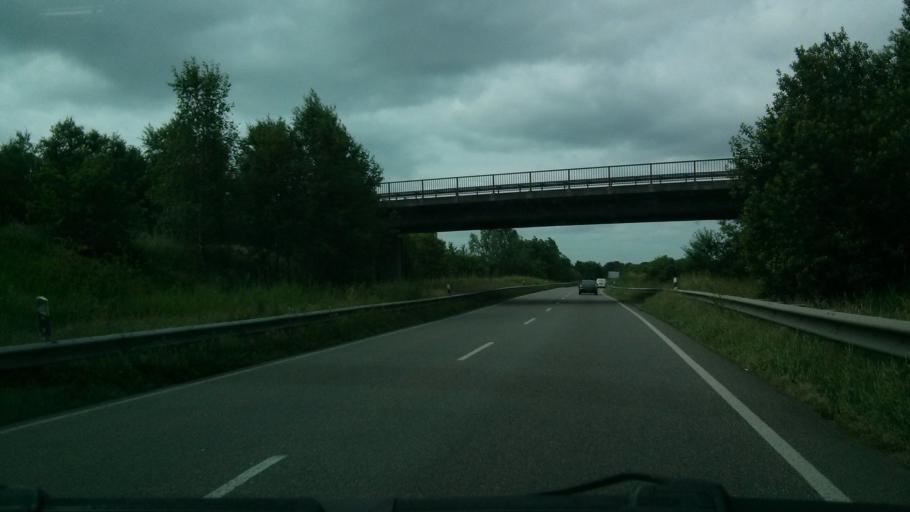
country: DE
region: Lower Saxony
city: Driftsethe
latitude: 53.4389
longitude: 8.5714
